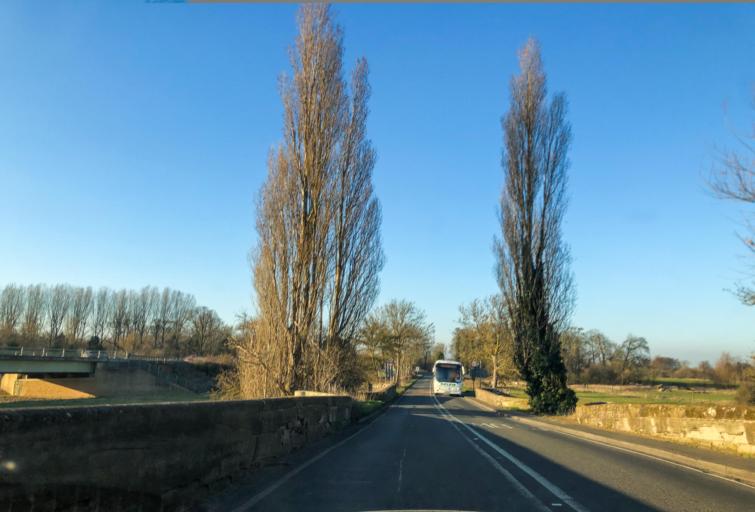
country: GB
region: England
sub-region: Warwickshire
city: Warwick
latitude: 52.2464
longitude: -1.6092
